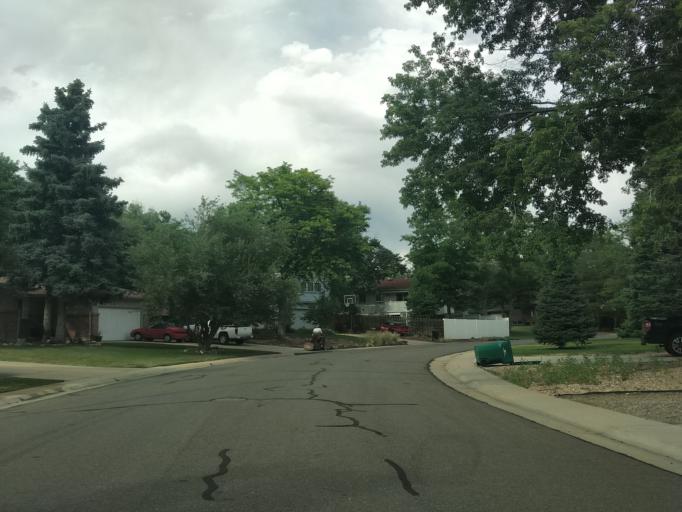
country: US
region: Colorado
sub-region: Jefferson County
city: Lakewood
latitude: 39.6991
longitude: -105.1048
